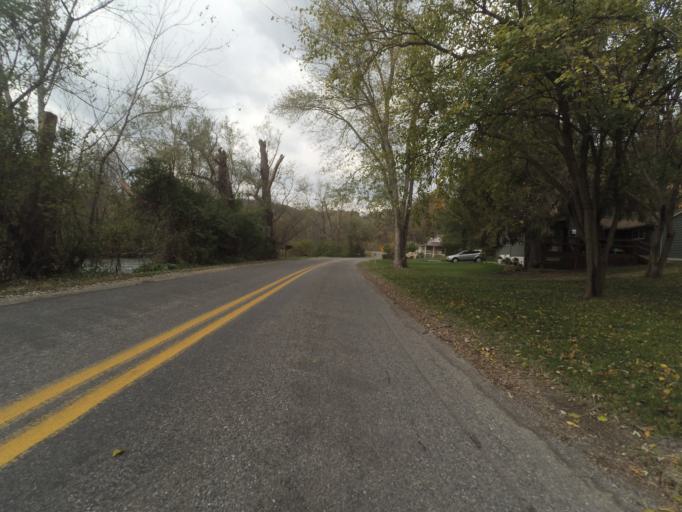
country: US
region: Pennsylvania
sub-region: Centre County
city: Bellefonte
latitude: 40.8889
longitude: -77.7919
